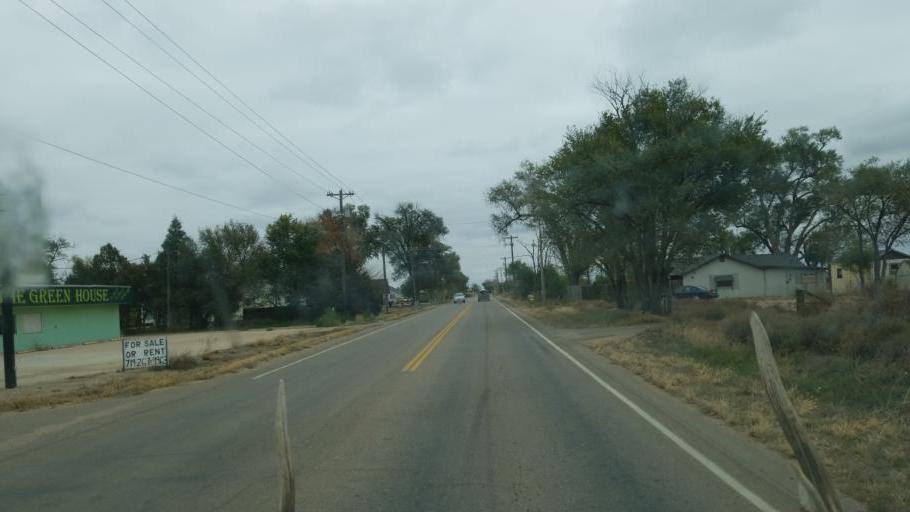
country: US
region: Colorado
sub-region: Crowley County
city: Ordway
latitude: 38.2145
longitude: -103.7541
